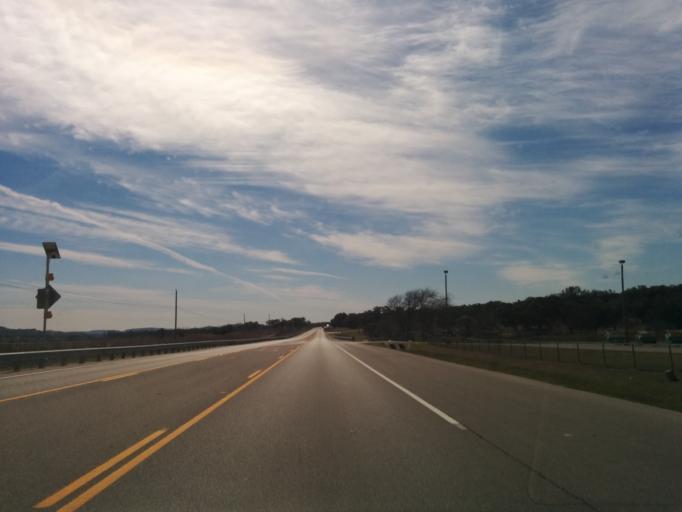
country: US
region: Texas
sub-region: Bexar County
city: Fair Oaks Ranch
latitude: 29.7281
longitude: -98.6235
